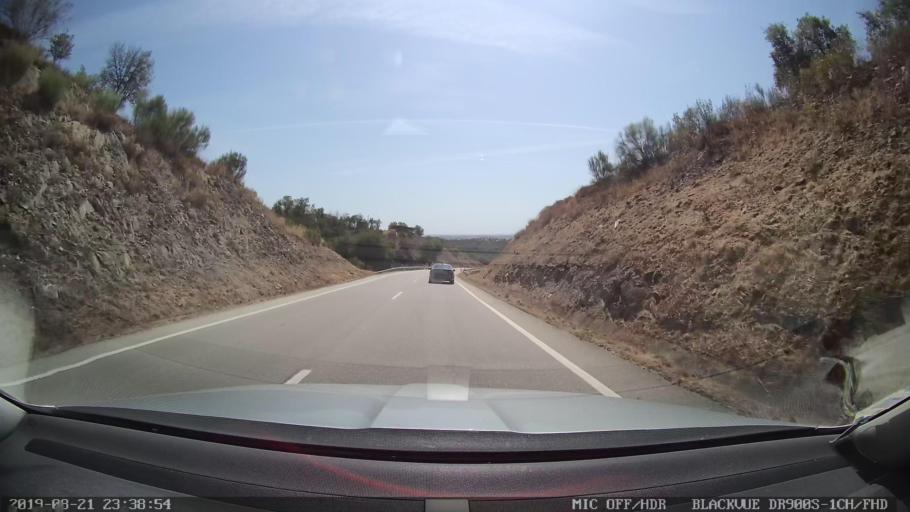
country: PT
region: Castelo Branco
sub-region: Idanha-A-Nova
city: Idanha-a-Nova
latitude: 39.8590
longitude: -7.3452
